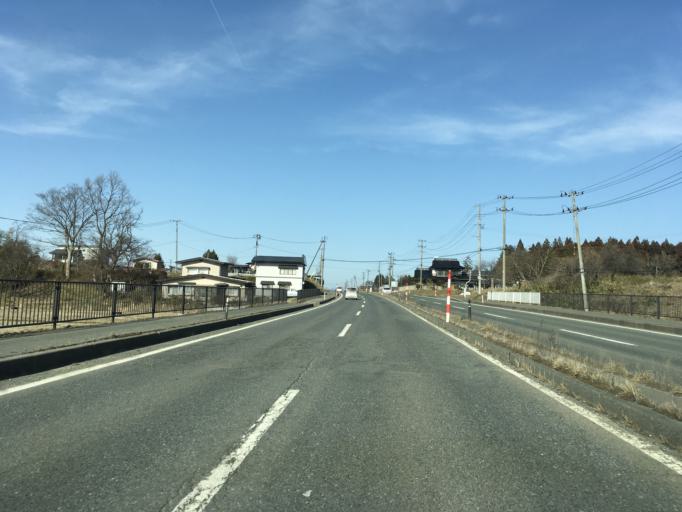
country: JP
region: Iwate
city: Hanamaki
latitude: 39.5228
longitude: 141.1617
